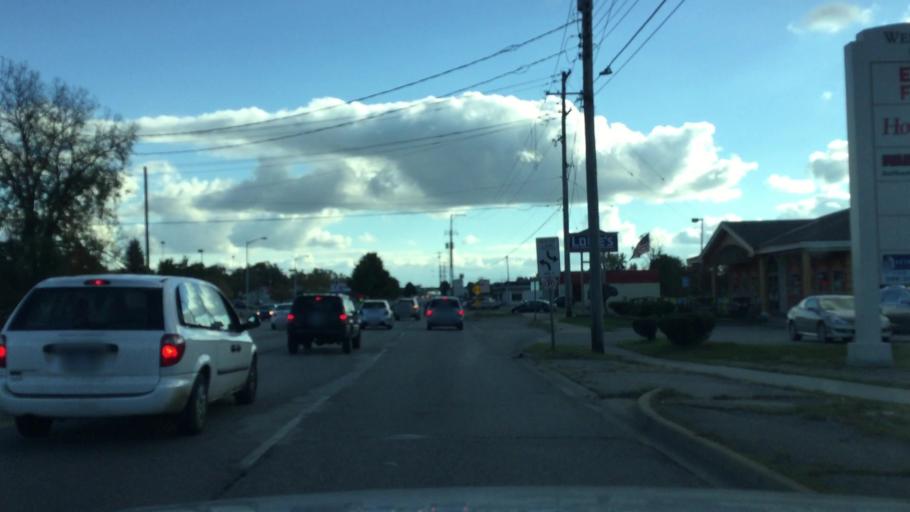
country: US
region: Michigan
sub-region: Kalamazoo County
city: Portage
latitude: 42.2444
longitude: -85.5897
